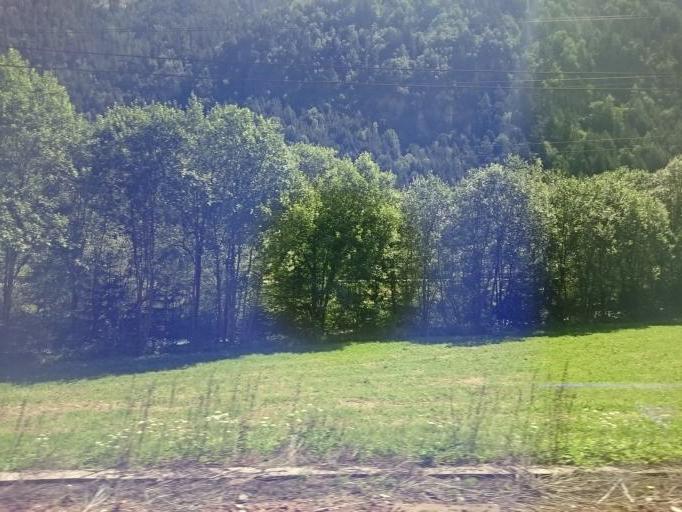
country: IT
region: Trentino-Alto Adige
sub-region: Bolzano
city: Campo di Trens
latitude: 46.8267
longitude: 11.5355
